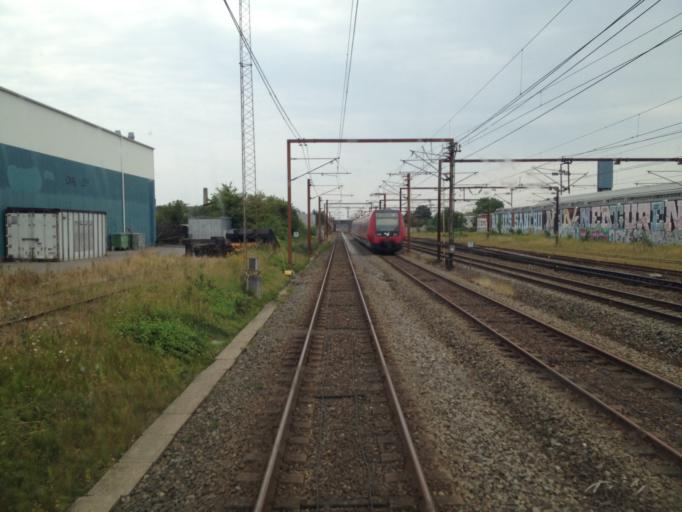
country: DK
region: Capital Region
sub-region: Albertslund Kommune
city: Albertslund
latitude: 55.6614
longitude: 12.3830
